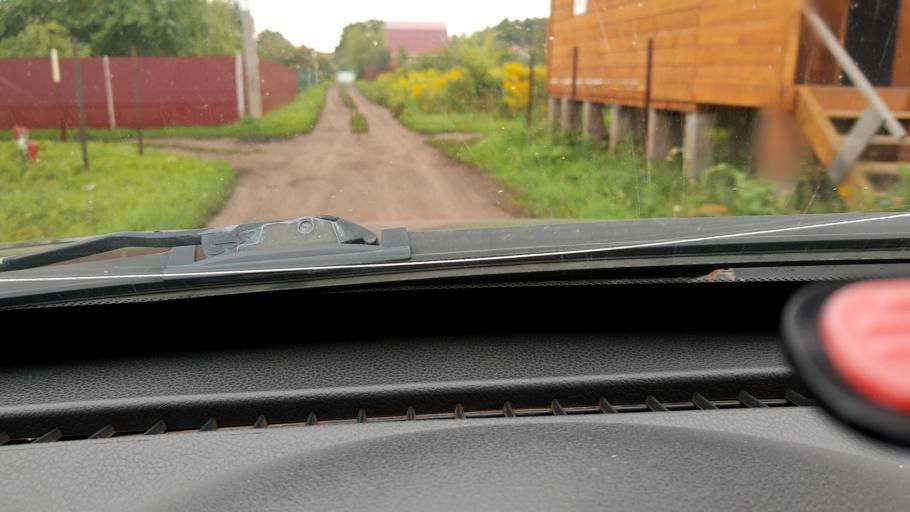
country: RU
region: Bashkortostan
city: Kabakovo
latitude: 54.7185
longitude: 56.1775
